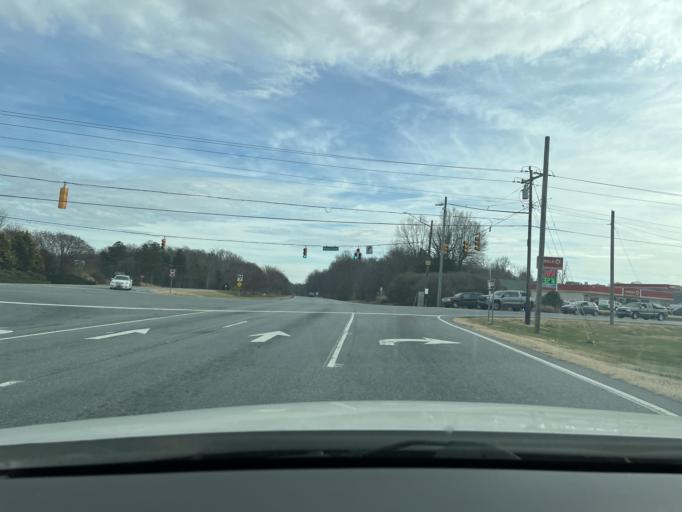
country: US
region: North Carolina
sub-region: Guilford County
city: Greensboro
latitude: 36.0280
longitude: -79.7707
